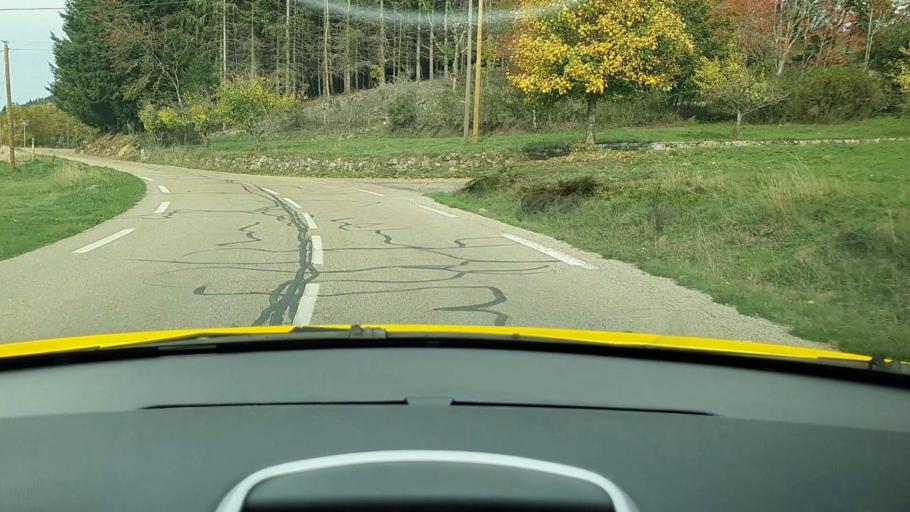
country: FR
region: Languedoc-Roussillon
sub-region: Departement de la Lozere
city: Meyrueis
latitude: 44.1210
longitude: 3.4842
